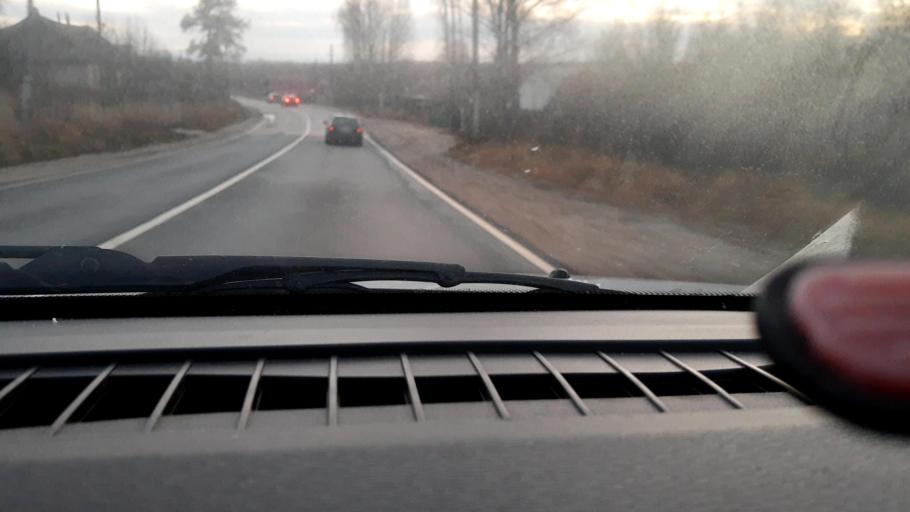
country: RU
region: Nizjnij Novgorod
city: Krasnyye Baki
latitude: 57.0694
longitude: 45.1383
